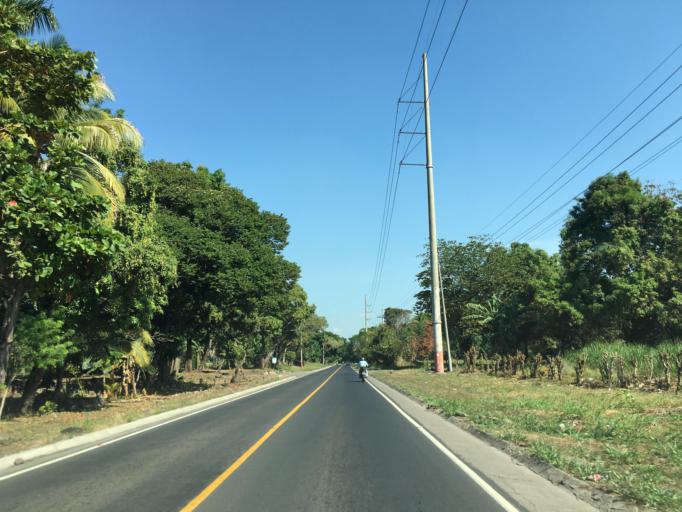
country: GT
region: Escuintla
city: Siquinala
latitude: 14.2900
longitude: -90.9691
